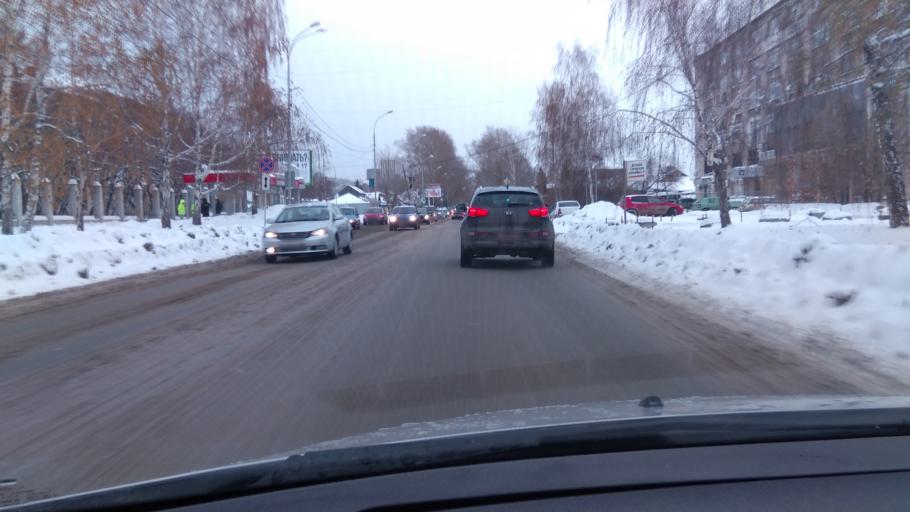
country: RU
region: Sverdlovsk
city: Yekaterinburg
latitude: 56.8121
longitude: 60.5769
